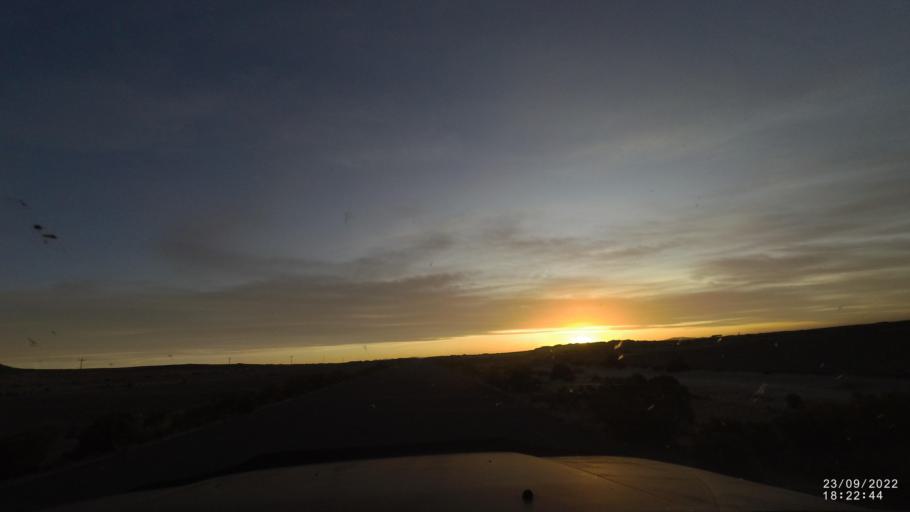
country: BO
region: Oruro
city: Challapata
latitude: -19.2904
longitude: -67.0910
